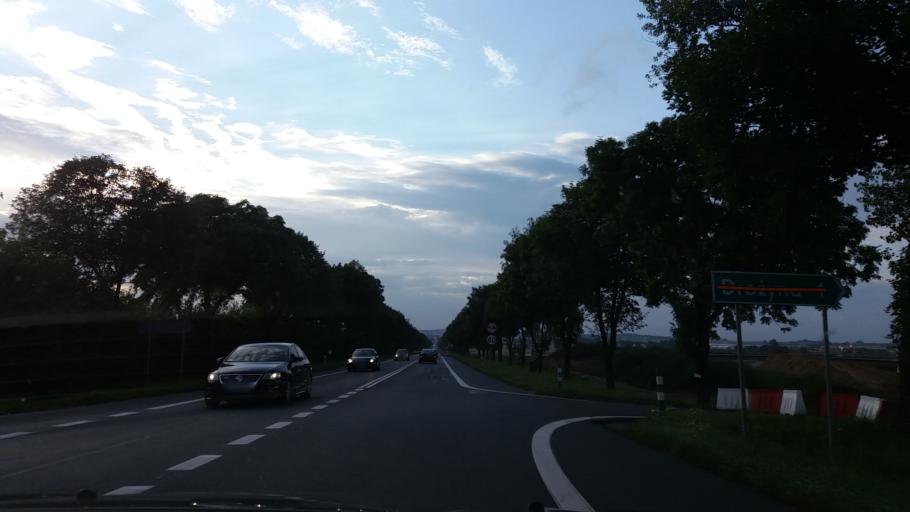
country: PL
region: Lower Silesian Voivodeship
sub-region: Powiat polkowicki
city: Radwanice
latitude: 51.6044
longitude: 15.9519
